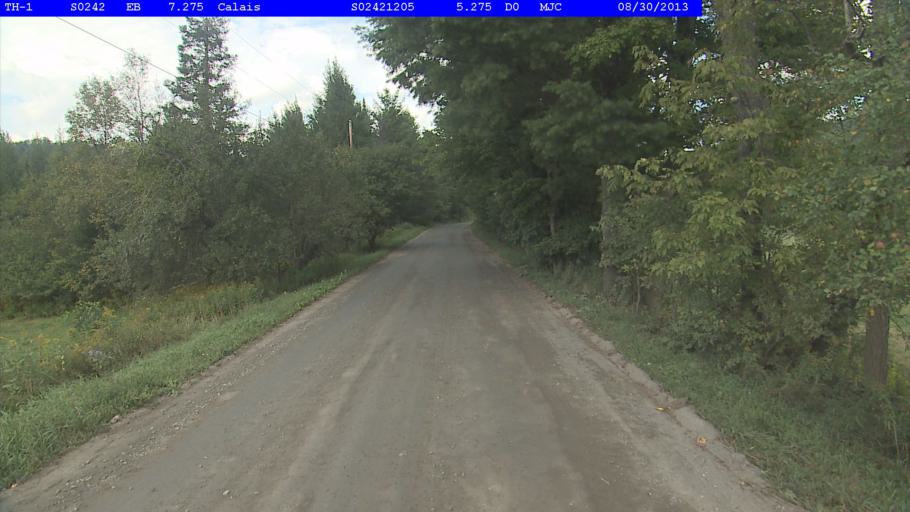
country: US
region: Vermont
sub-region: Caledonia County
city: Hardwick
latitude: 44.3810
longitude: -72.4553
